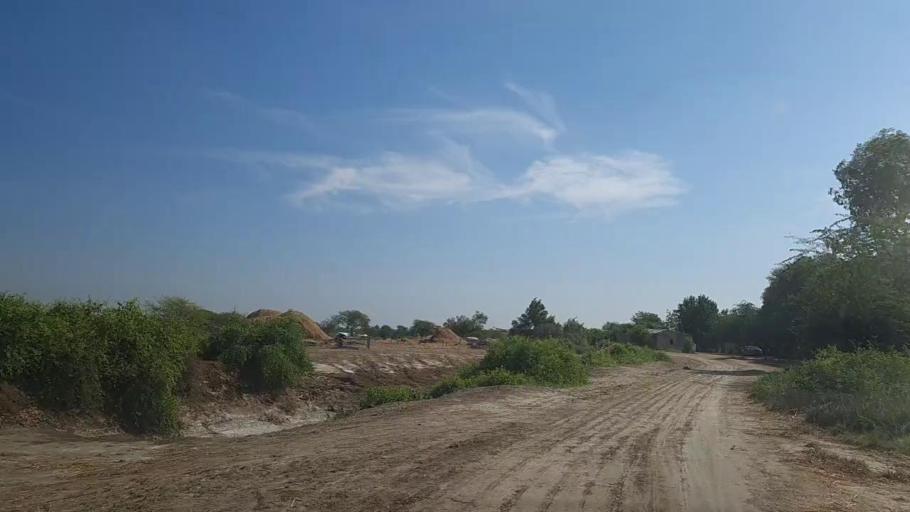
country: PK
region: Sindh
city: Mirpur Batoro
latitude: 24.7597
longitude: 68.2978
